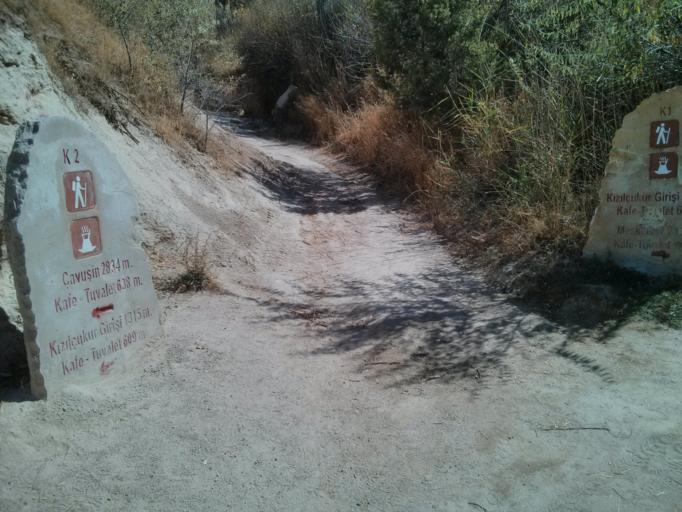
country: TR
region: Nevsehir
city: Goereme
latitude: 38.6510
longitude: 34.8498
